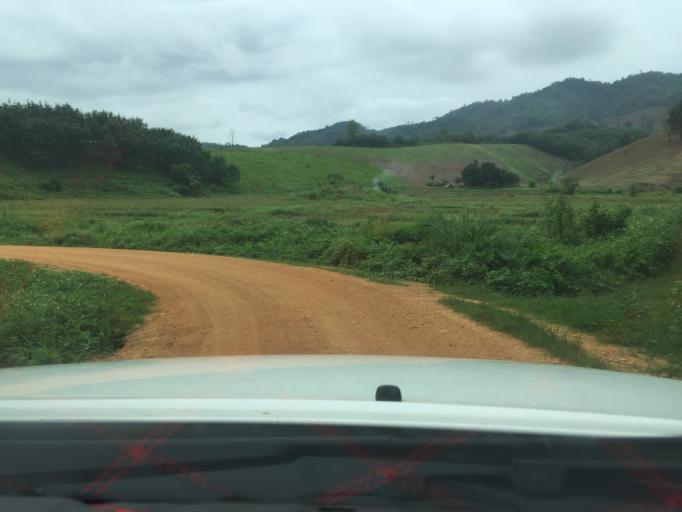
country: TH
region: Phayao
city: Phu Sang
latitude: 19.7694
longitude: 100.5521
